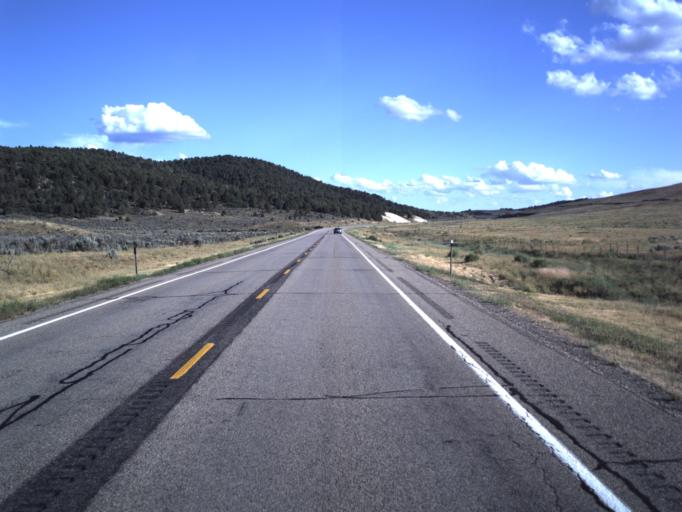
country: US
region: Utah
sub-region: Sanpete County
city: Fairview
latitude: 39.7510
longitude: -111.4790
